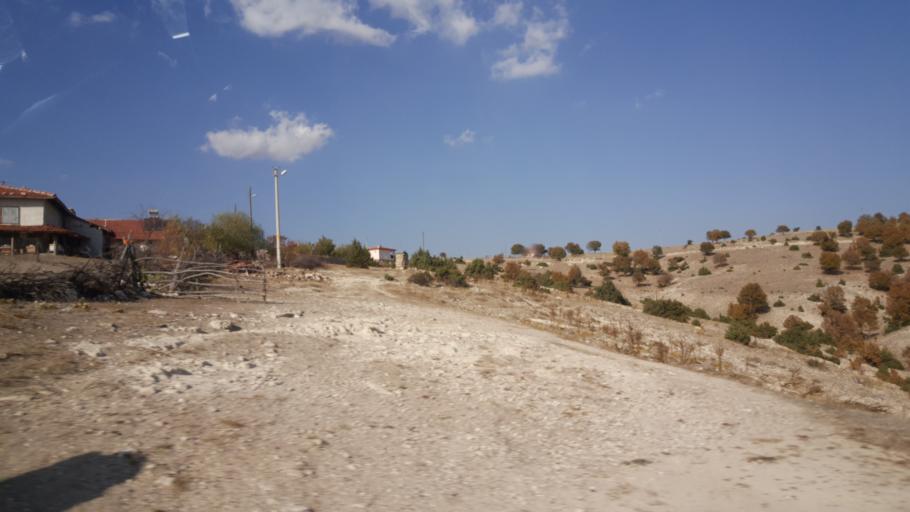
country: TR
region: Eskisehir
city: Kirka
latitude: 39.3246
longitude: 30.5660
